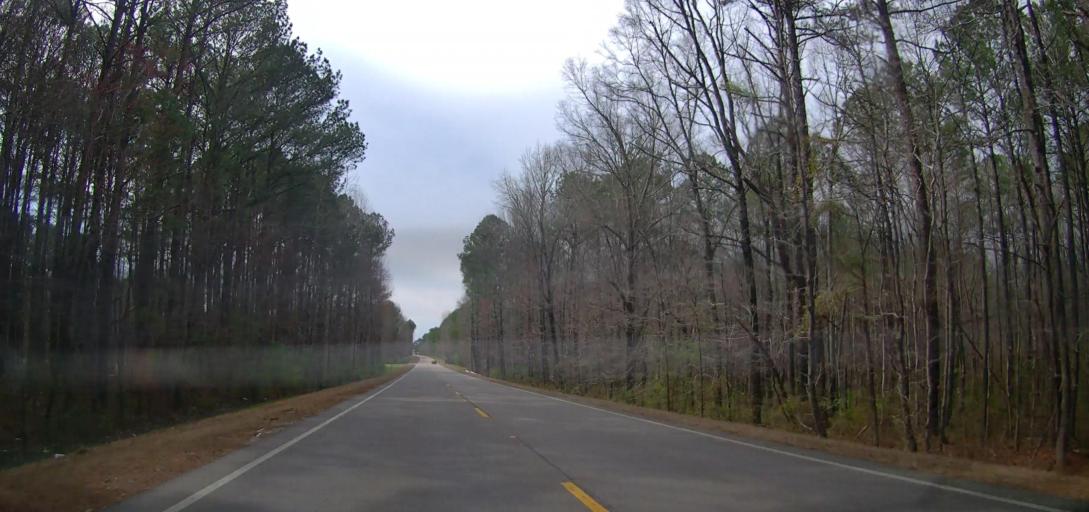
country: US
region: Alabama
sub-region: Walker County
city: Carbon Hill
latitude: 33.8754
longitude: -87.4658
